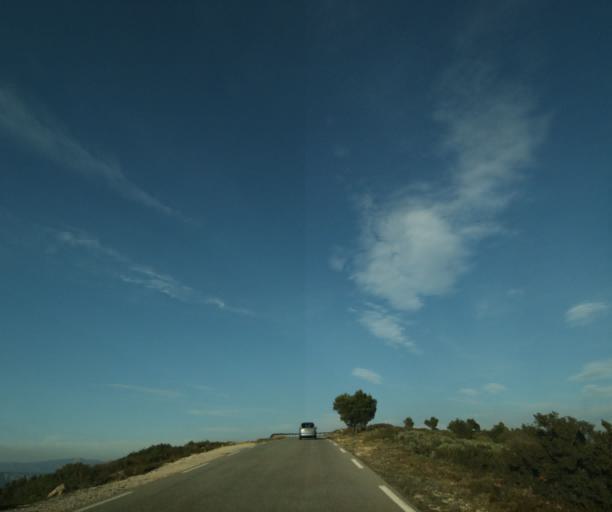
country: FR
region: Provence-Alpes-Cote d'Azur
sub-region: Departement des Bouches-du-Rhone
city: Cassis
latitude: 43.2001
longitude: 5.5544
